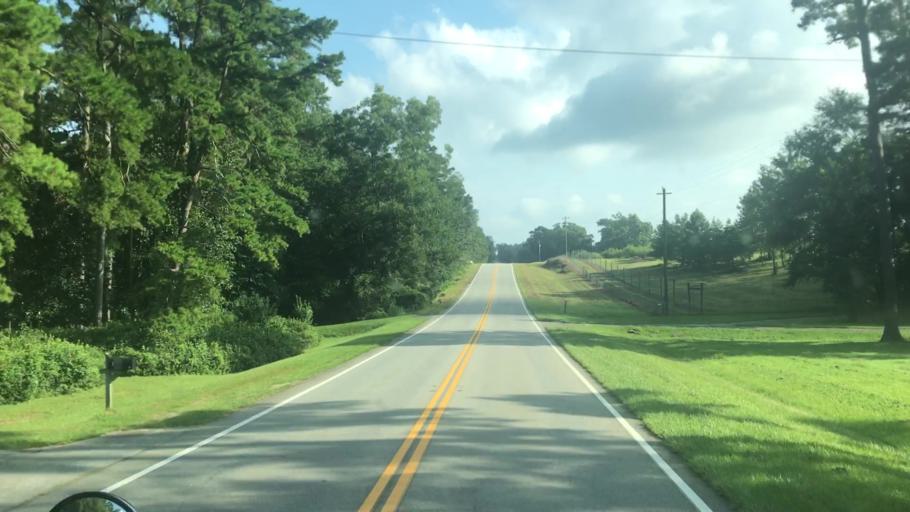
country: US
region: Florida
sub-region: Gadsden County
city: Havana
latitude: 30.7615
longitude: -84.4879
